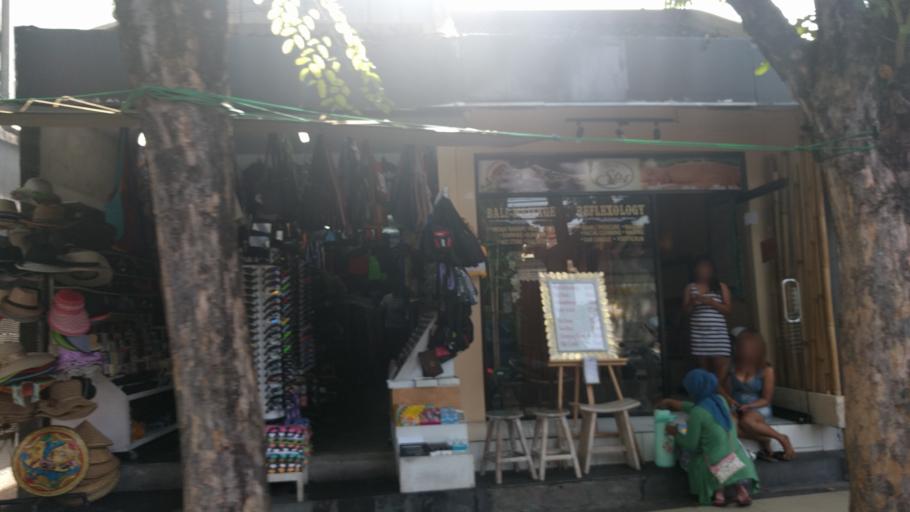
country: ID
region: Bali
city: Kuta
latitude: -8.7200
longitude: 115.1750
